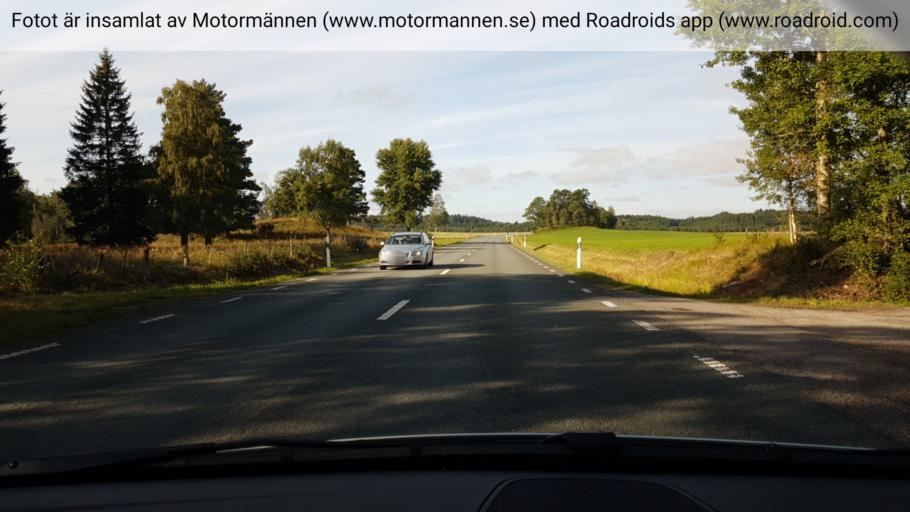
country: SE
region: Vaestra Goetaland
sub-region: Tidaholms Kommun
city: Tidaholm
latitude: 58.1332
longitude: 13.8746
